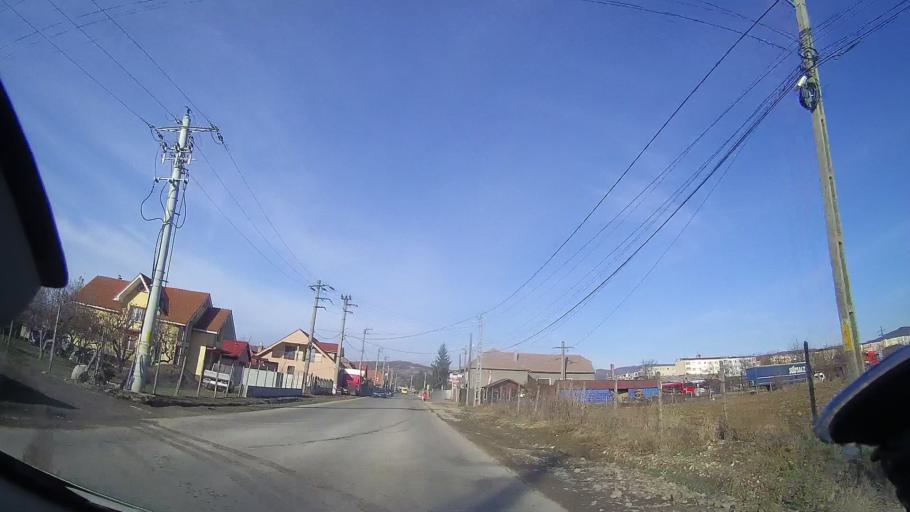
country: RO
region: Bihor
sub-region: Comuna Astileu
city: Astileu
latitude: 47.0529
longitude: 22.3920
